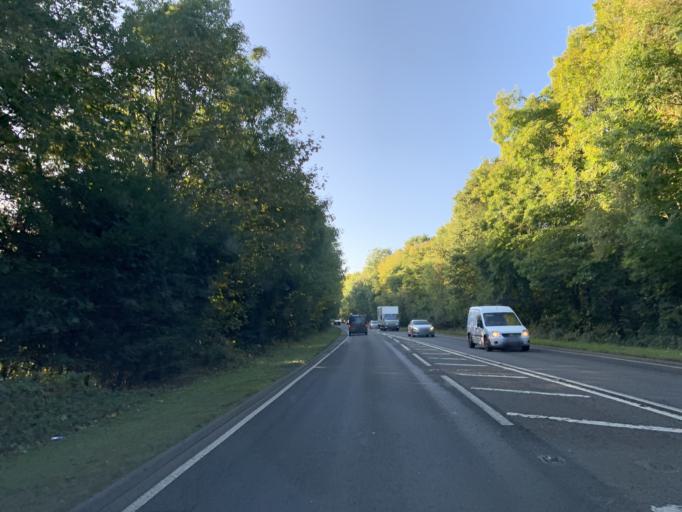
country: GB
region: England
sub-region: Wiltshire
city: Whiteparish
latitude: 50.9864
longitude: -1.6410
